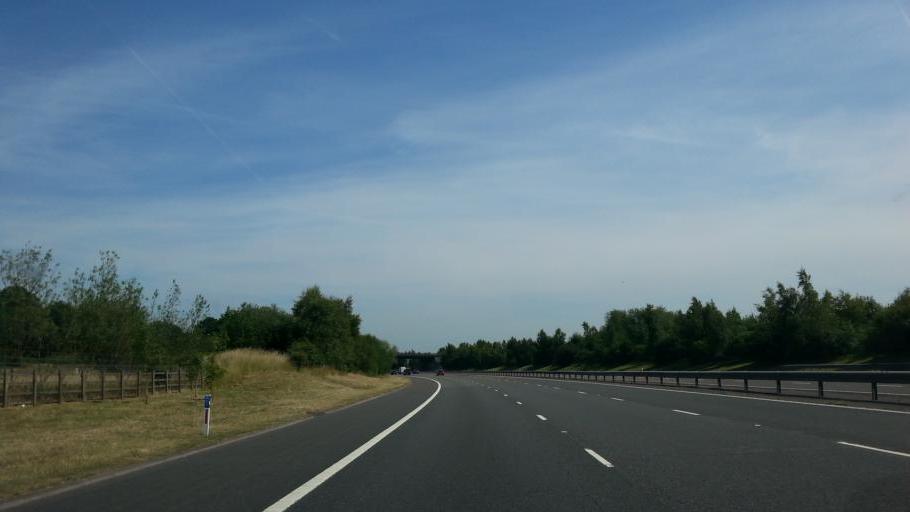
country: GB
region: England
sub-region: Staffordshire
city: Chasetown
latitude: 52.6522
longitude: -1.8958
